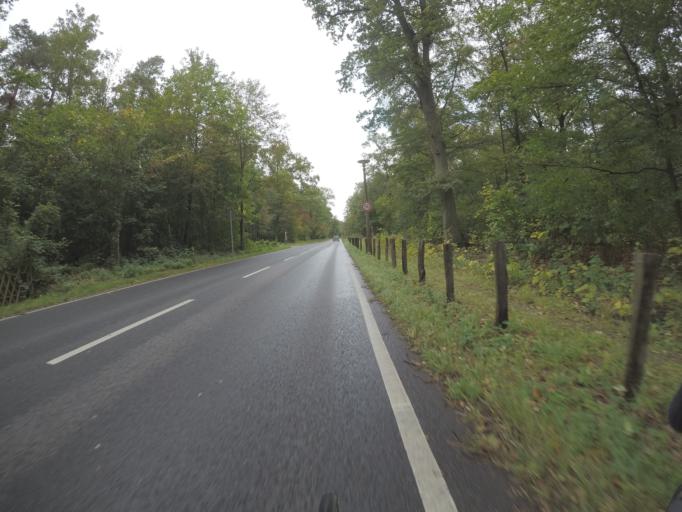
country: DE
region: Berlin
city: Buch
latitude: 52.6466
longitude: 13.4827
